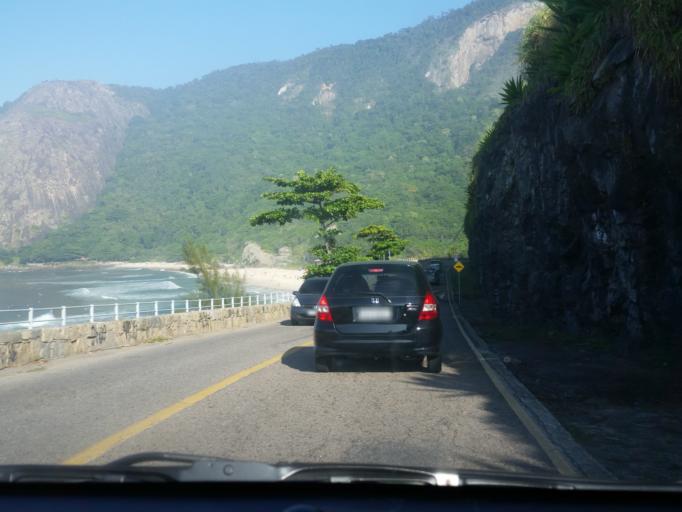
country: BR
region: Rio de Janeiro
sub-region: Nilopolis
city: Nilopolis
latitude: -23.0400
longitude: -43.5012
